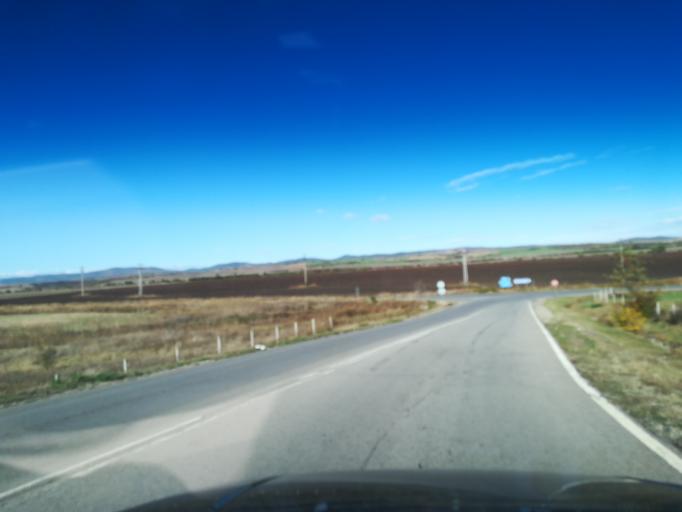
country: BG
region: Stara Zagora
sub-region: Obshtina Chirpan
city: Chirpan
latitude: 42.2078
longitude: 25.3006
